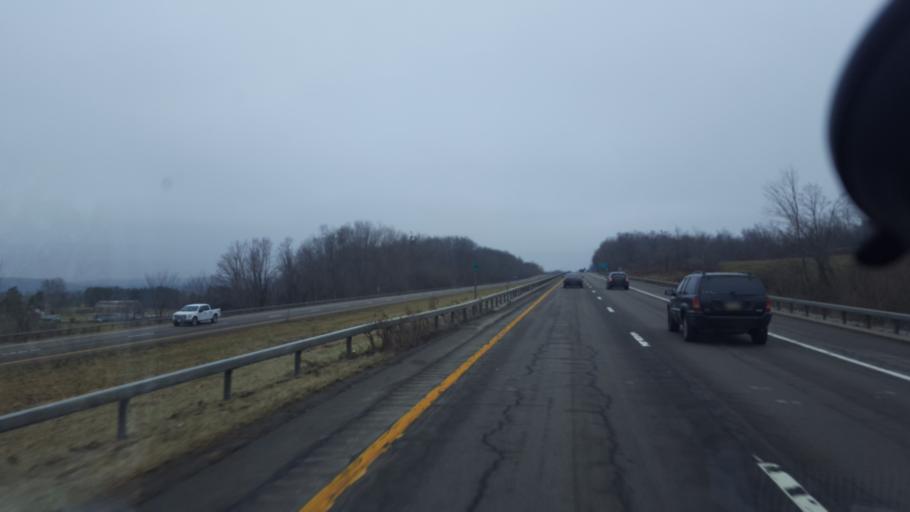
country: US
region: New York
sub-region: Cattaraugus County
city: Randolph
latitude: 42.1624
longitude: -79.0224
